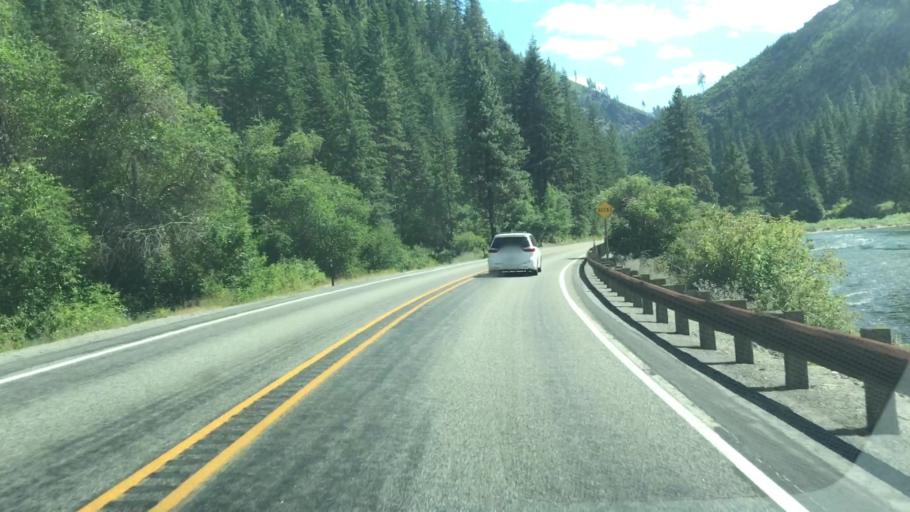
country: US
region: Washington
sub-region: Chelan County
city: Leavenworth
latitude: 47.6506
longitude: -120.7240
